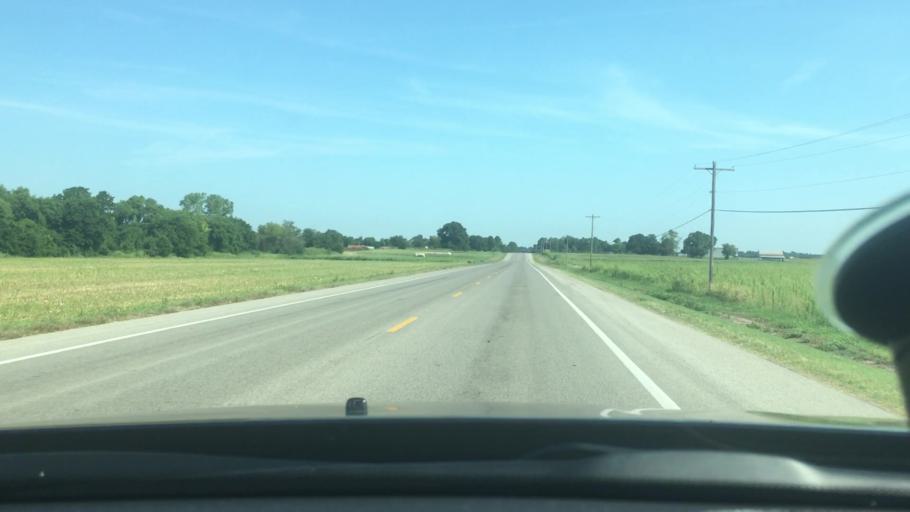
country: US
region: Oklahoma
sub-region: Garvin County
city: Wynnewood
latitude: 34.6572
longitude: -97.2021
